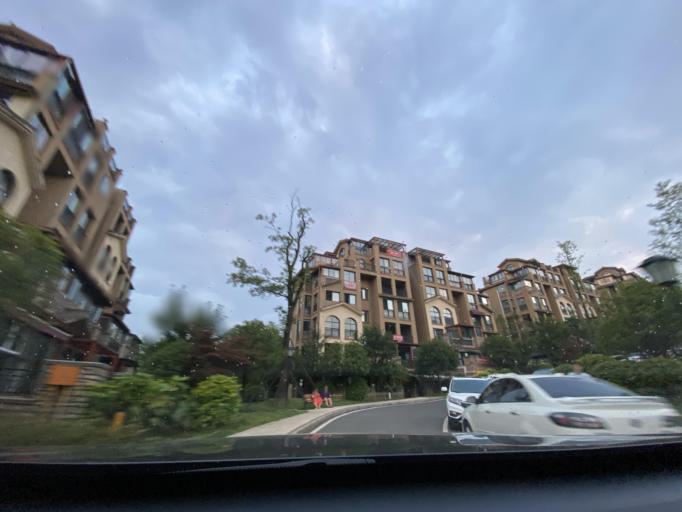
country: CN
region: Guizhou Sheng
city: Changqi
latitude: 28.5406
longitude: 105.9859
